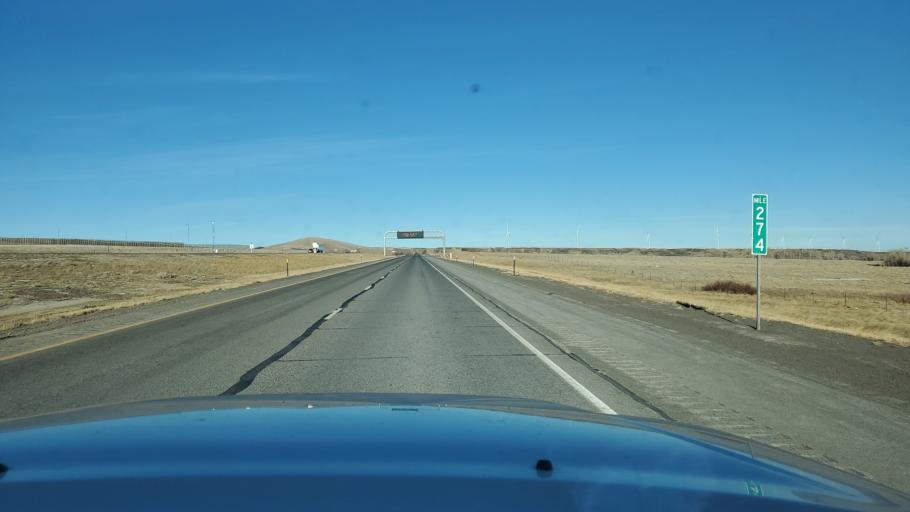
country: US
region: Wyoming
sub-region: Carbon County
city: Saratoga
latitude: 41.5863
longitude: -106.1764
